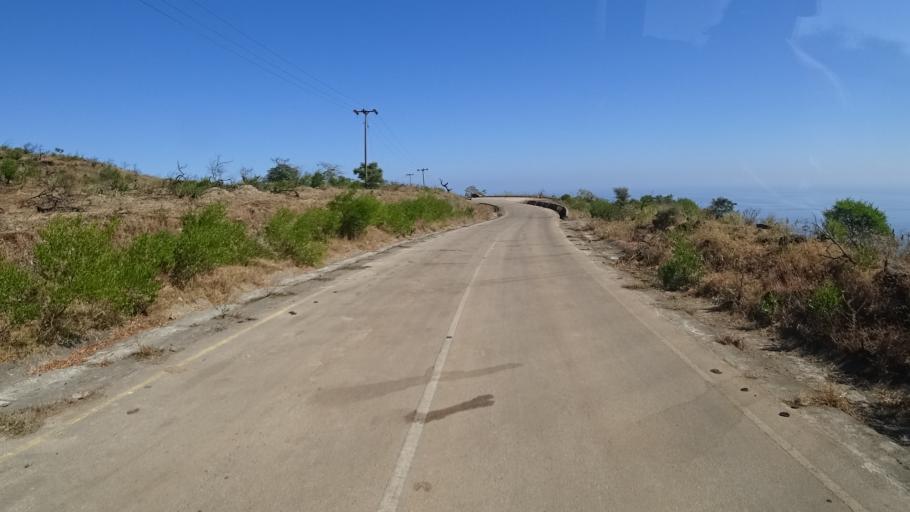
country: YE
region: Al Mahrah
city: Hawf
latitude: 16.7418
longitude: 53.3643
